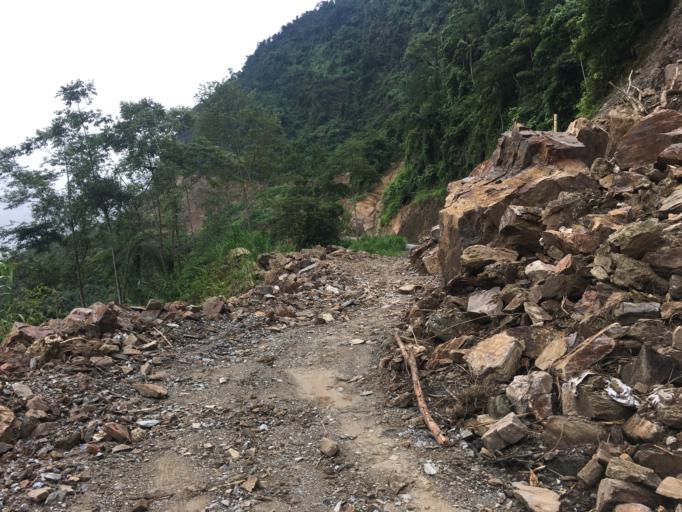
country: VN
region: Ha Giang
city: Thi Tran Tam Son
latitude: 22.9806
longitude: 105.0604
